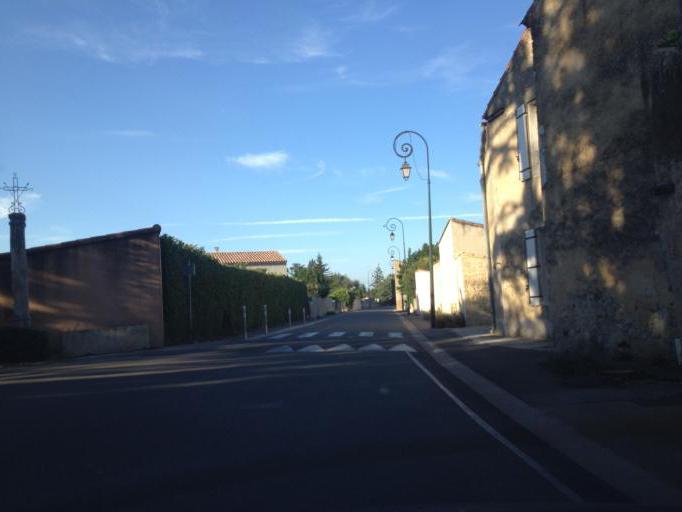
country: FR
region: Provence-Alpes-Cote d'Azur
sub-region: Departement du Vaucluse
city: Camaret-sur-Aigues
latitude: 44.1661
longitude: 4.8743
